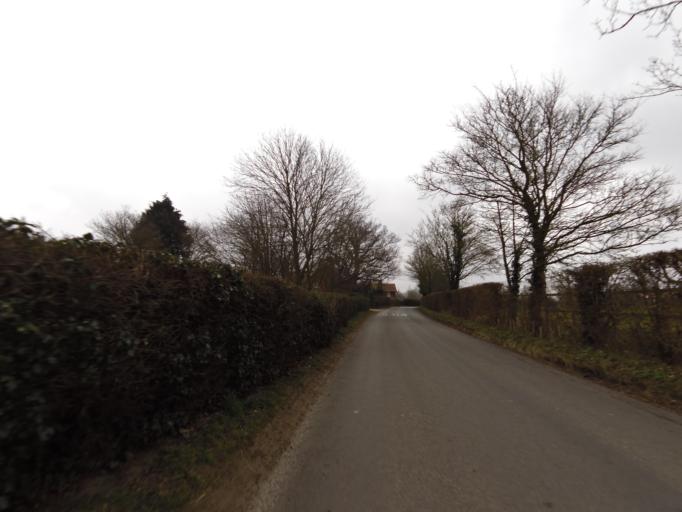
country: GB
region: England
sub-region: Suffolk
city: Framlingham
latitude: 52.1904
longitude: 1.3356
